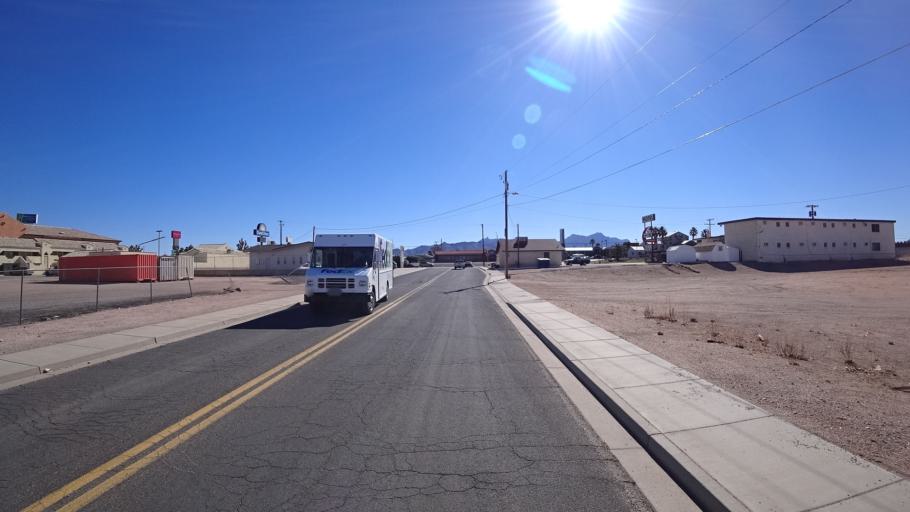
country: US
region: Arizona
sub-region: Mohave County
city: Kingman
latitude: 35.2137
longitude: -114.0156
